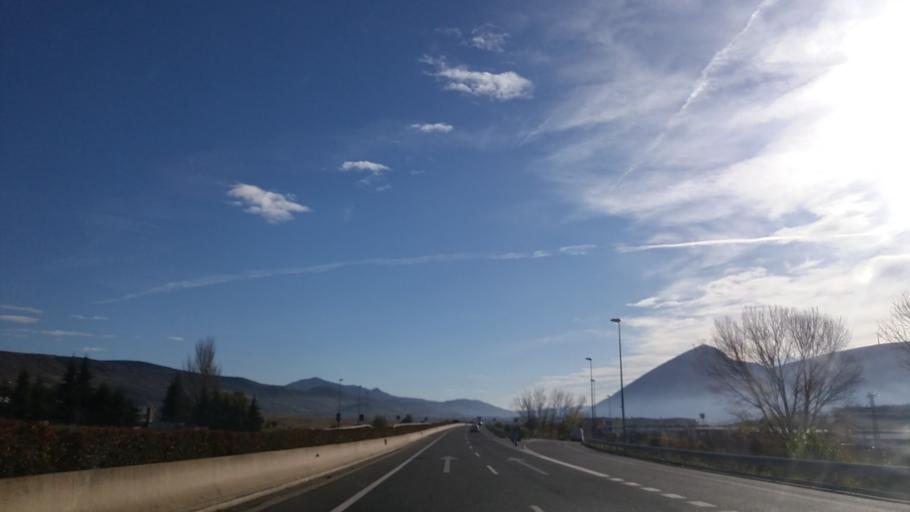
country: ES
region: Navarre
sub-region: Provincia de Navarra
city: Elorz
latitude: 42.7485
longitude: -1.6025
